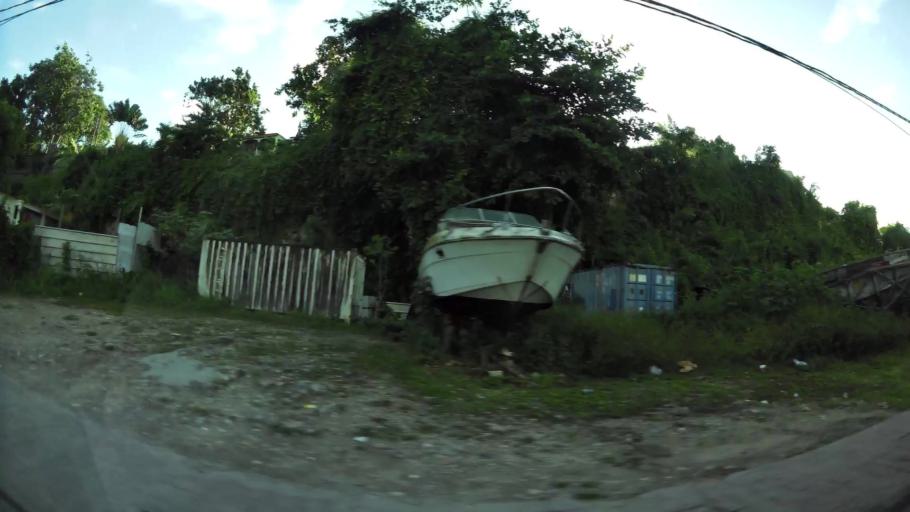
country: GP
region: Guadeloupe
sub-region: Guadeloupe
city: Pointe-a-Pitre
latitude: 16.2286
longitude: -61.5315
